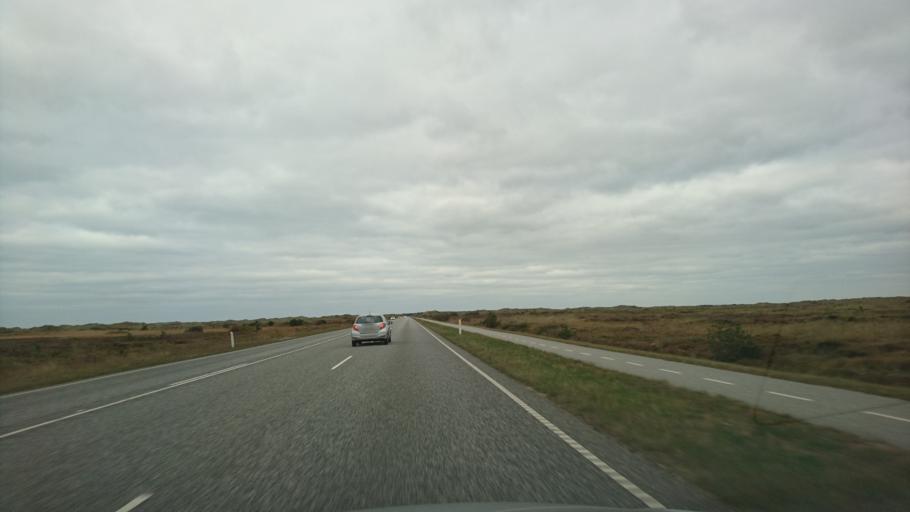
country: DK
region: North Denmark
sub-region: Frederikshavn Kommune
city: Skagen
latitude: 57.6775
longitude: 10.4598
